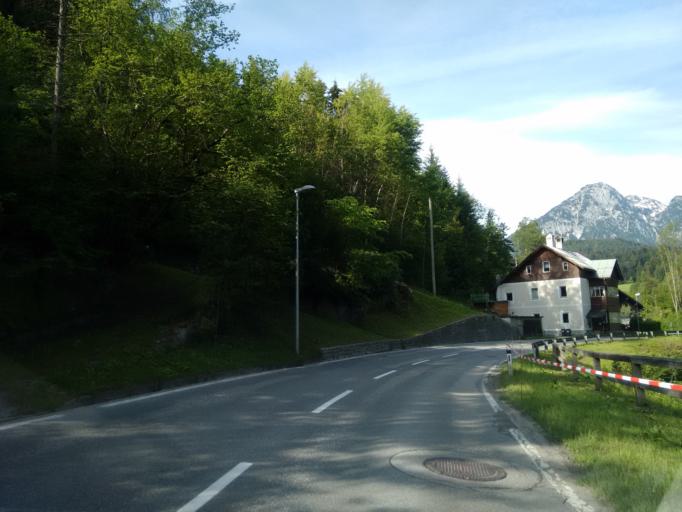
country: AT
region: Styria
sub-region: Politischer Bezirk Liezen
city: Altaussee
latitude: 47.6307
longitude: 13.7645
